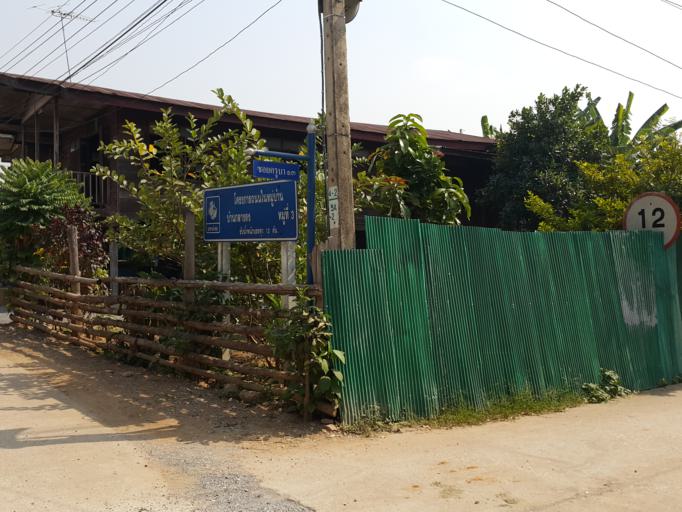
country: TH
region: Sukhothai
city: Thung Saliam
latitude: 17.3252
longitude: 99.5141
